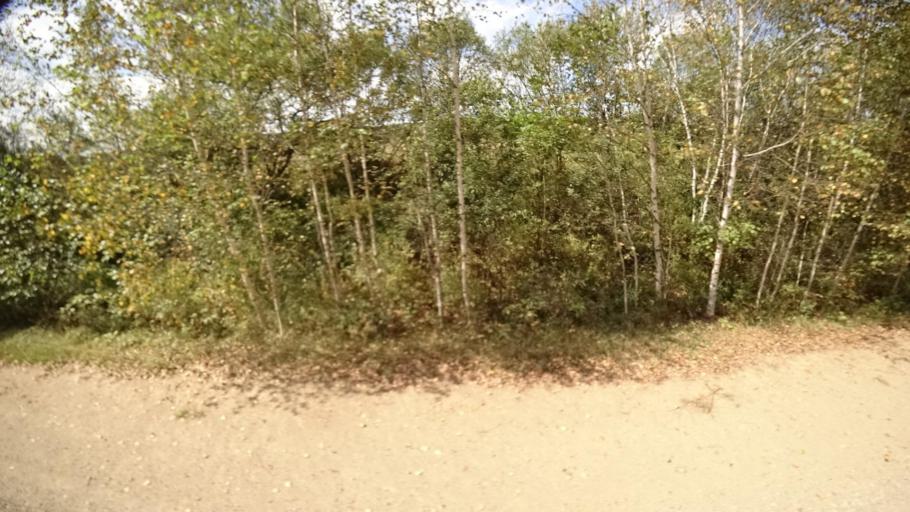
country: RU
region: Primorskiy
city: Yakovlevka
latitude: 44.6856
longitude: 133.6179
